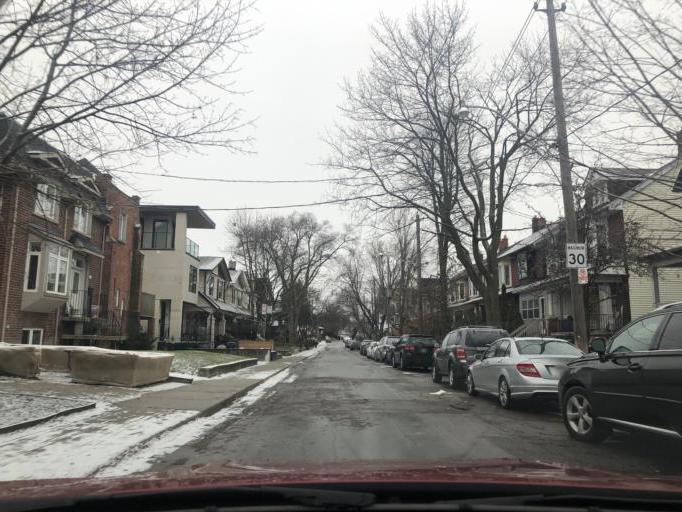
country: CA
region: Ontario
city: Toronto
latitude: 43.6779
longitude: -79.3417
